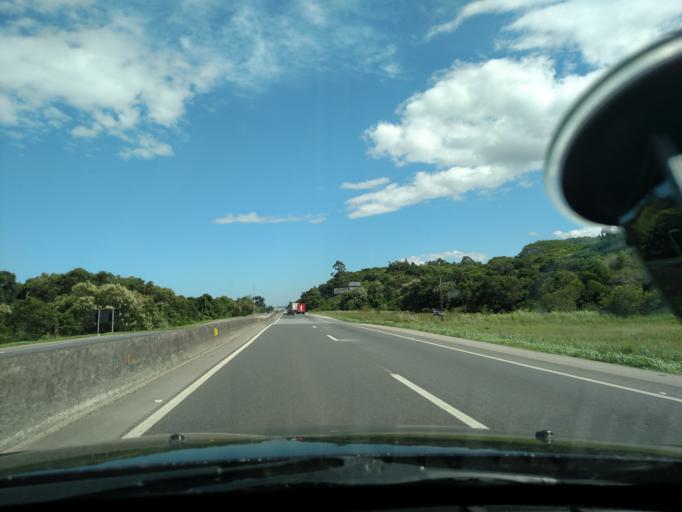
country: BR
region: Santa Catarina
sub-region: Biguacu
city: Biguacu
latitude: -27.4106
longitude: -48.6277
